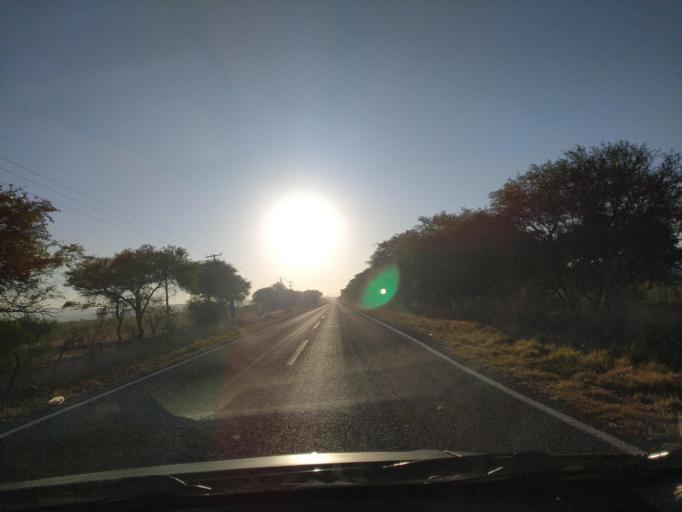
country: MX
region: Guanajuato
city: Ciudad Manuel Doblado
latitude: 20.7371
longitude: -101.8583
